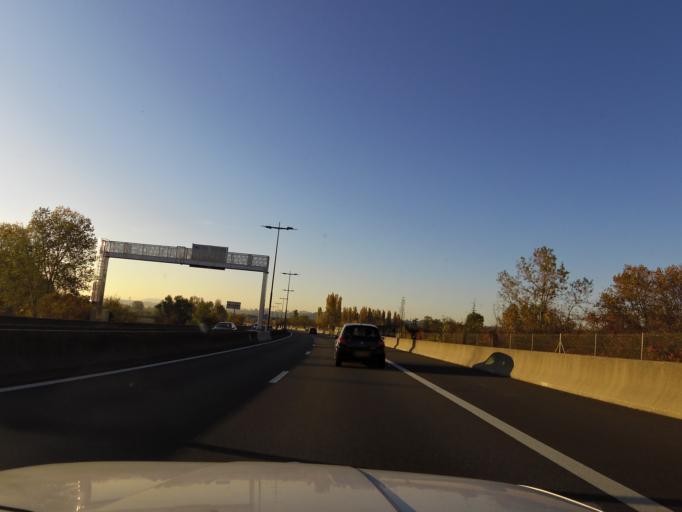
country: FR
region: Rhone-Alpes
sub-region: Departement du Rhone
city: Decines-Charpieu
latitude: 45.7930
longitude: 4.9533
